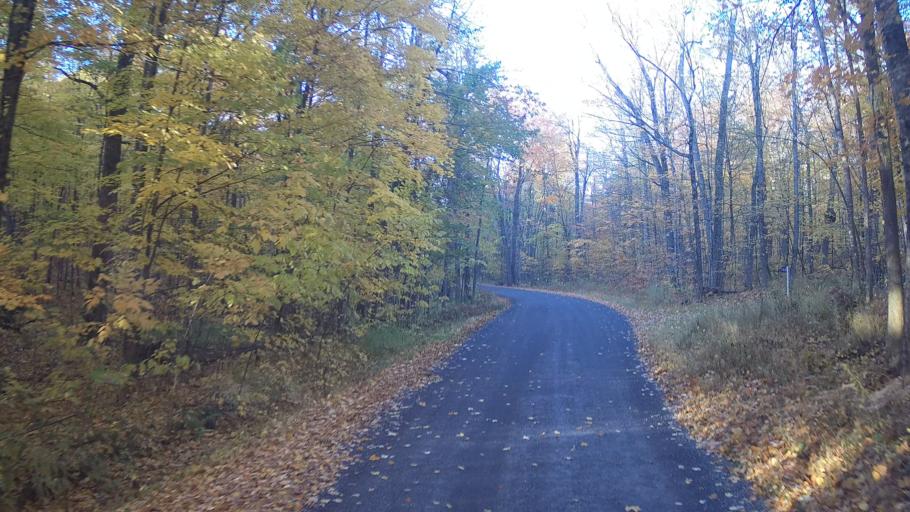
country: CA
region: Ontario
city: Arnprior
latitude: 45.3336
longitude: -76.3638
